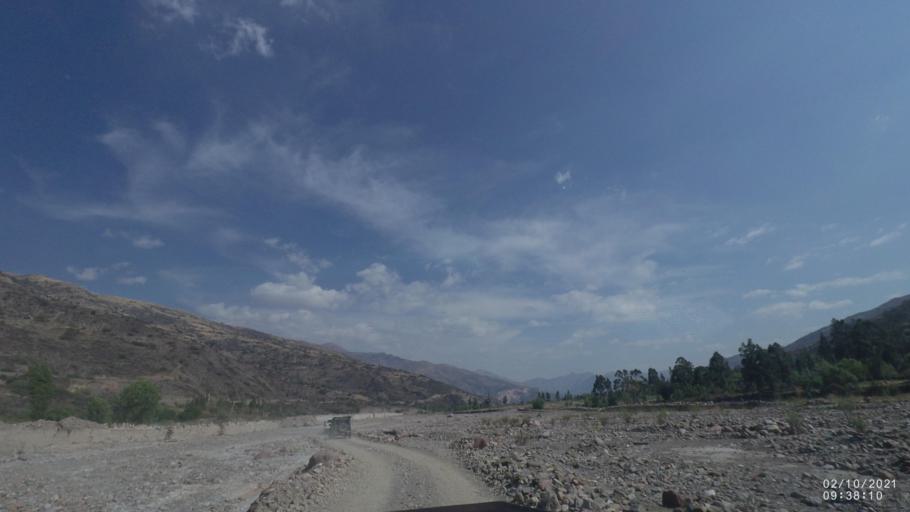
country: BO
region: Cochabamba
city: Irpa Irpa
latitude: -17.8288
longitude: -66.3246
